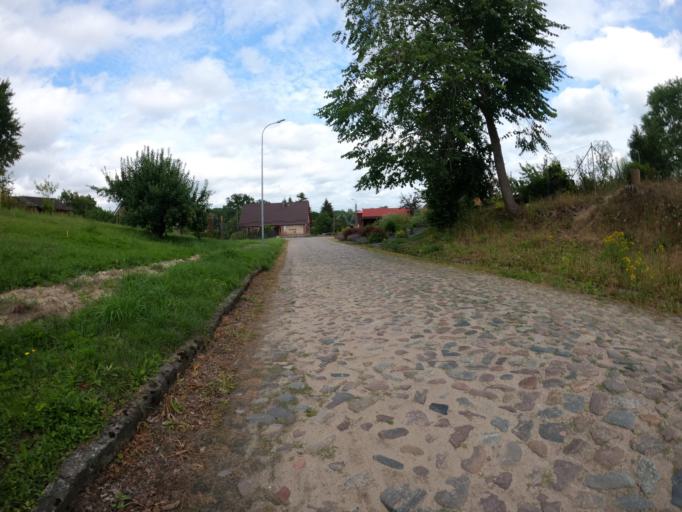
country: PL
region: West Pomeranian Voivodeship
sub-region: Powiat szczecinecki
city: Grzmiaca
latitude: 53.7961
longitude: 16.4731
